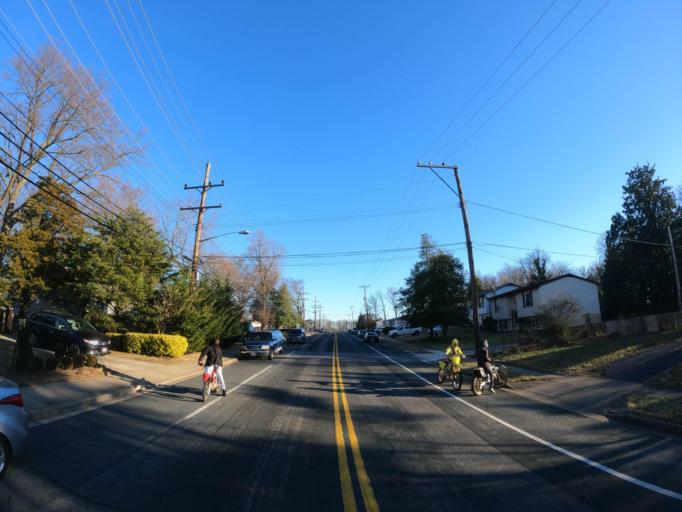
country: US
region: Maryland
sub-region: Prince George's County
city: Woodlawn
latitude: 38.9552
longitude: -76.8805
